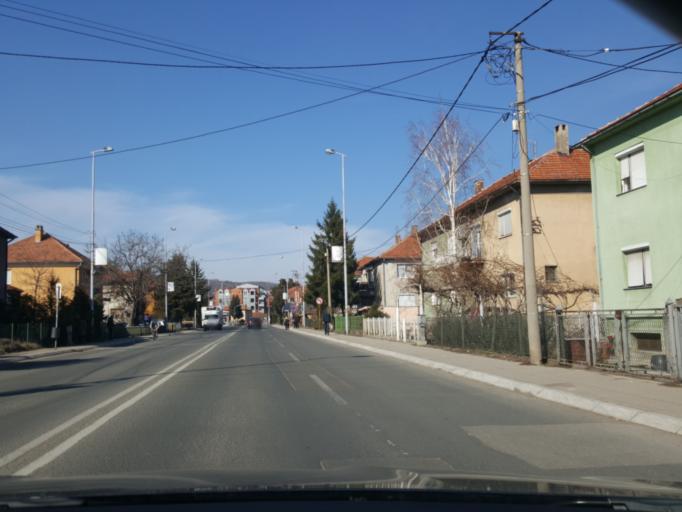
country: RS
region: Central Serbia
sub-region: Nisavski Okrug
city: Nis
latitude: 43.3279
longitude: 21.9253
